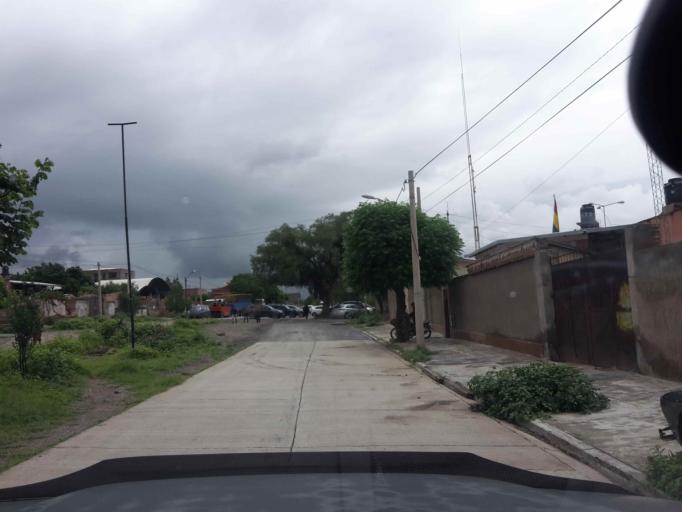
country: BO
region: Cochabamba
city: Cochabamba
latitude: -17.3773
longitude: -66.1194
